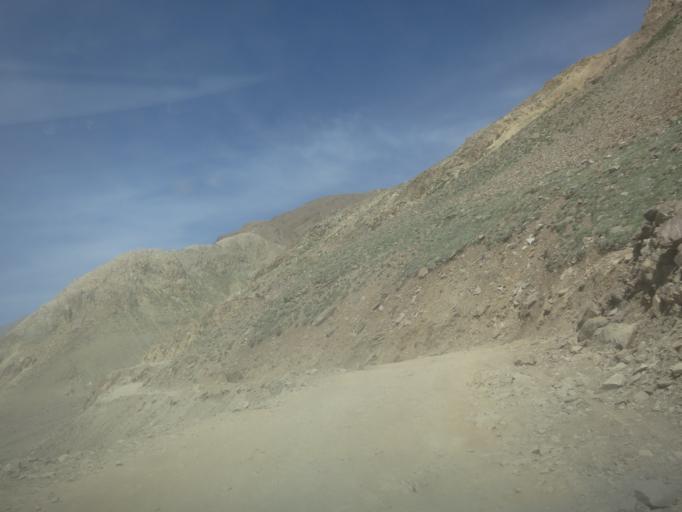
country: IN
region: Himachal Pradesh
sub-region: Kulu
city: Manali
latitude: 32.4268
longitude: 77.6694
